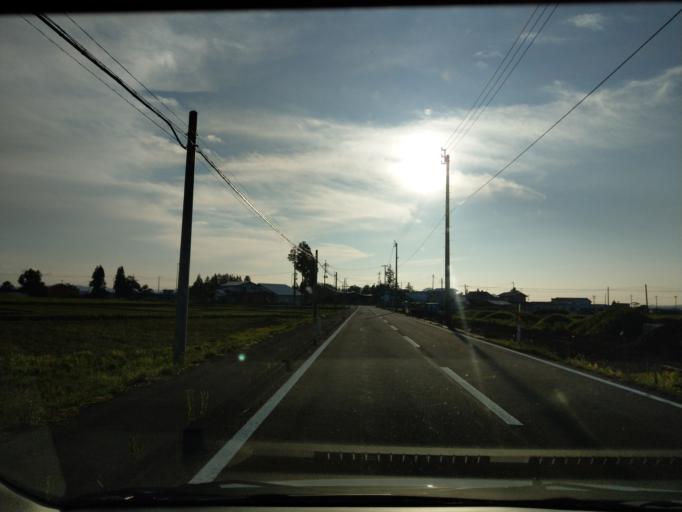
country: JP
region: Akita
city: Omagari
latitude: 39.4341
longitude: 140.5694
